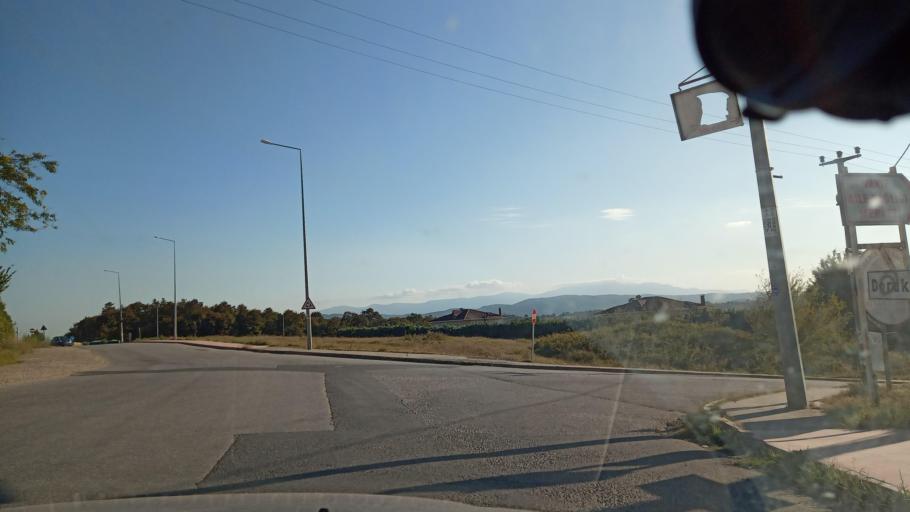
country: TR
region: Sakarya
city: Kazimpasa
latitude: 40.8513
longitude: 30.2790
